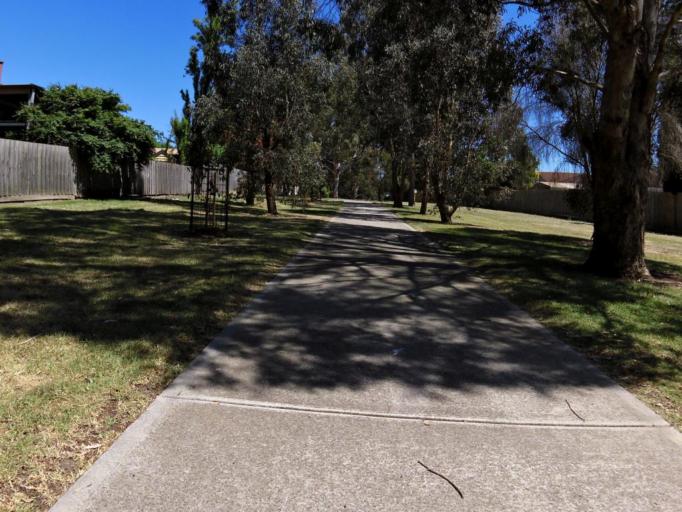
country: AU
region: Victoria
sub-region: Casey
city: Narre Warren
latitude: -38.0357
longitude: 145.3211
